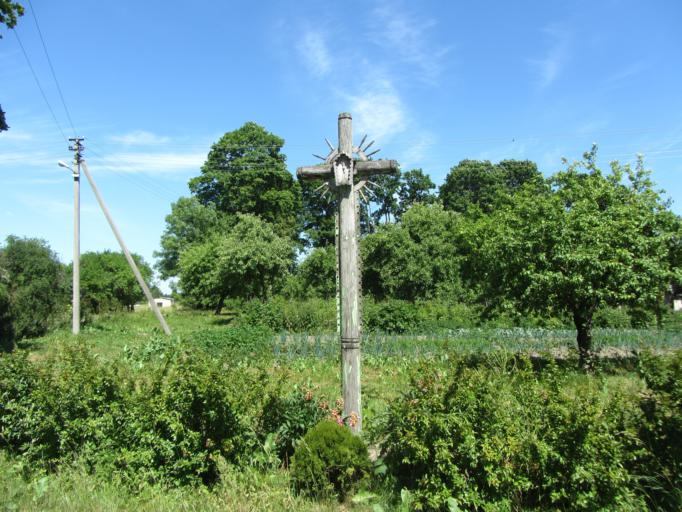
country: LT
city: Ziezmariai
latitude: 54.6968
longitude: 24.4359
